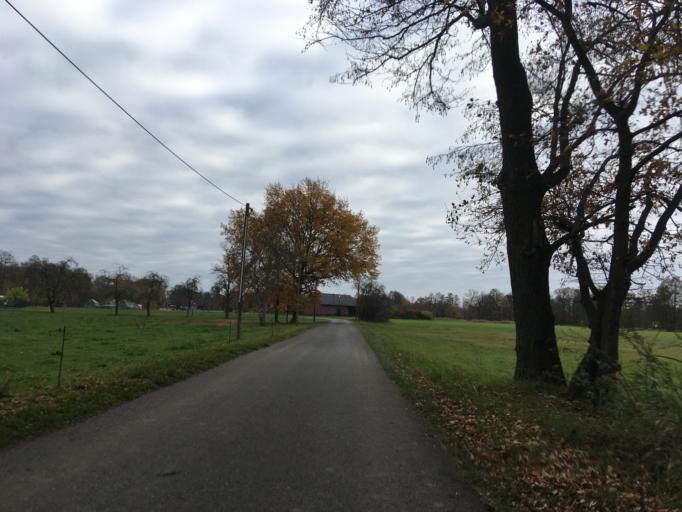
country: DE
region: Brandenburg
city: Burg
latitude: 51.8435
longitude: 14.1577
